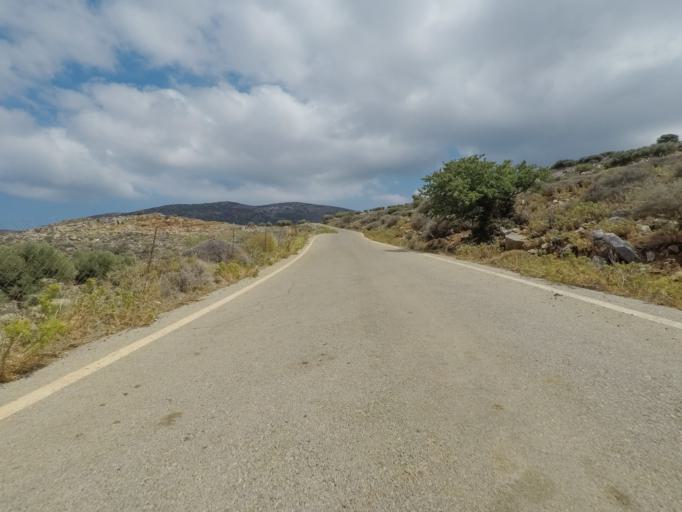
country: GR
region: Crete
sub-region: Nomos Lasithiou
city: Elounda
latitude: 35.3086
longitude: 25.6800
